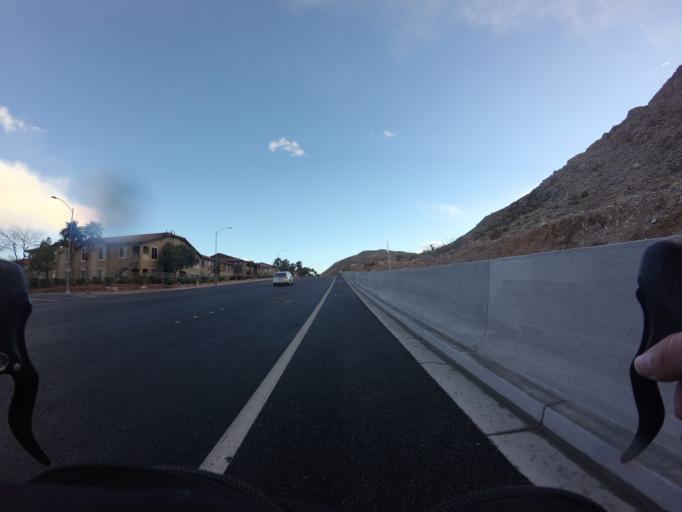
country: US
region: Nevada
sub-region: Clark County
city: Summerlin South
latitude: 36.2255
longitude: -115.3321
